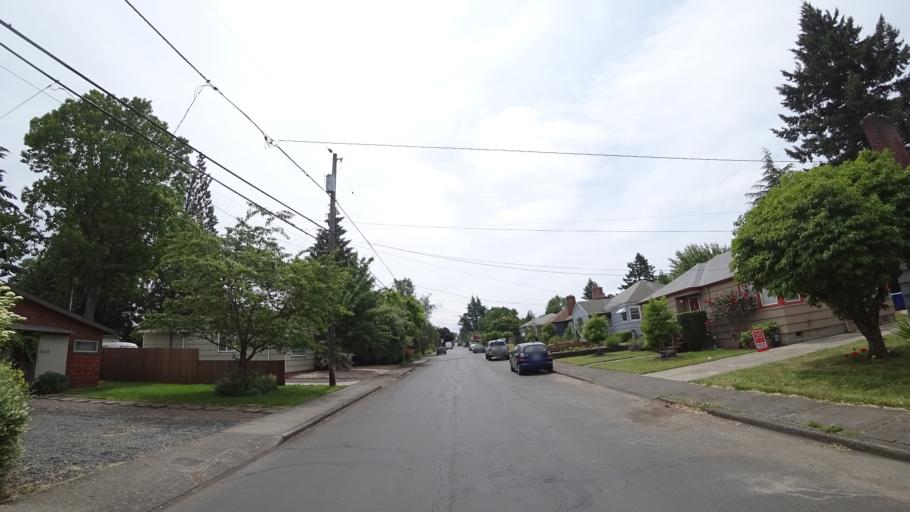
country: US
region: Oregon
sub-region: Multnomah County
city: Portland
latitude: 45.5608
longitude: -122.6255
